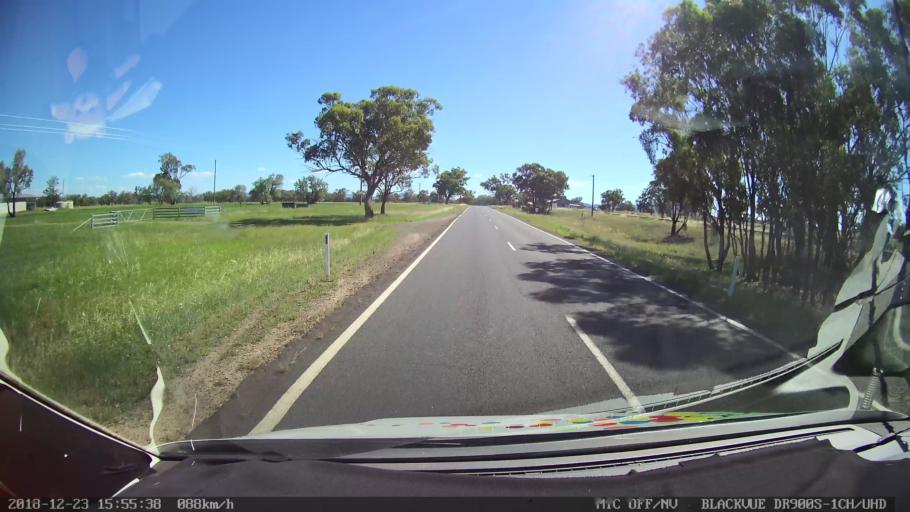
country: AU
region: New South Wales
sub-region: Tamworth Municipality
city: Phillip
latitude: -31.1574
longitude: 150.8664
